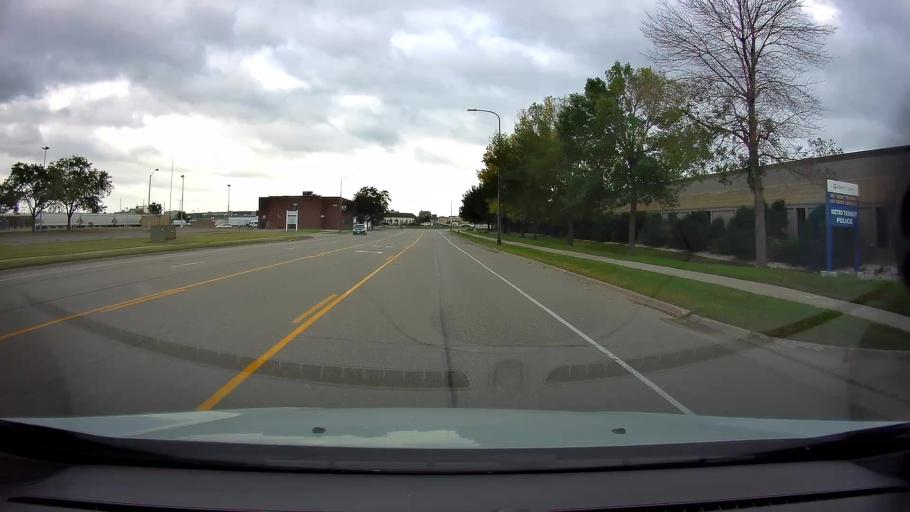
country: US
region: Minnesota
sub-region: Ramsey County
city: Falcon Heights
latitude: 44.9633
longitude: -93.1859
